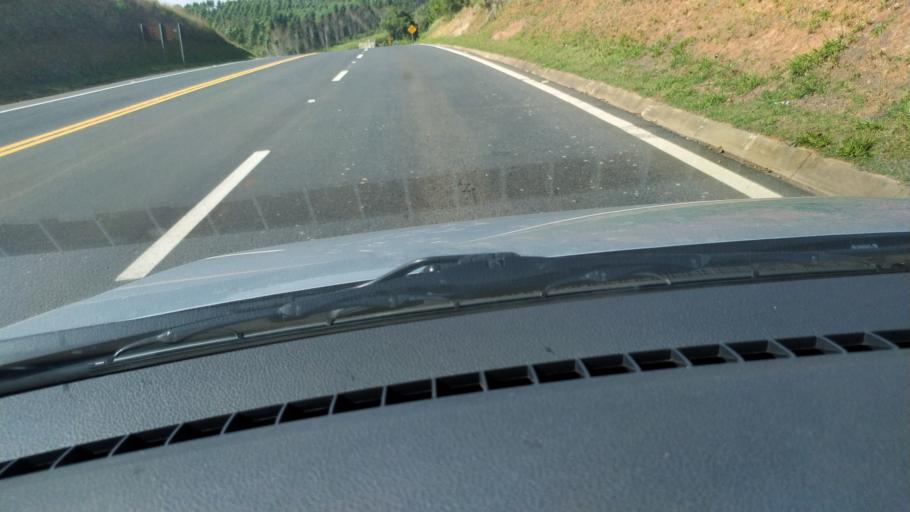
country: BR
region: Parana
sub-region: Telemaco Borba
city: Telemaco Borba
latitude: -24.3023
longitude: -50.7031
